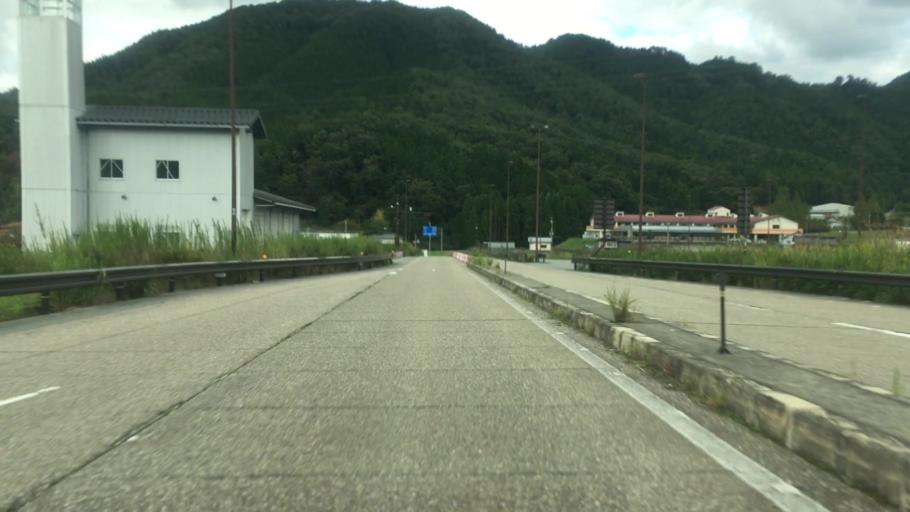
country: JP
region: Kyoto
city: Fukuchiyama
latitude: 35.3037
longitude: 134.9080
